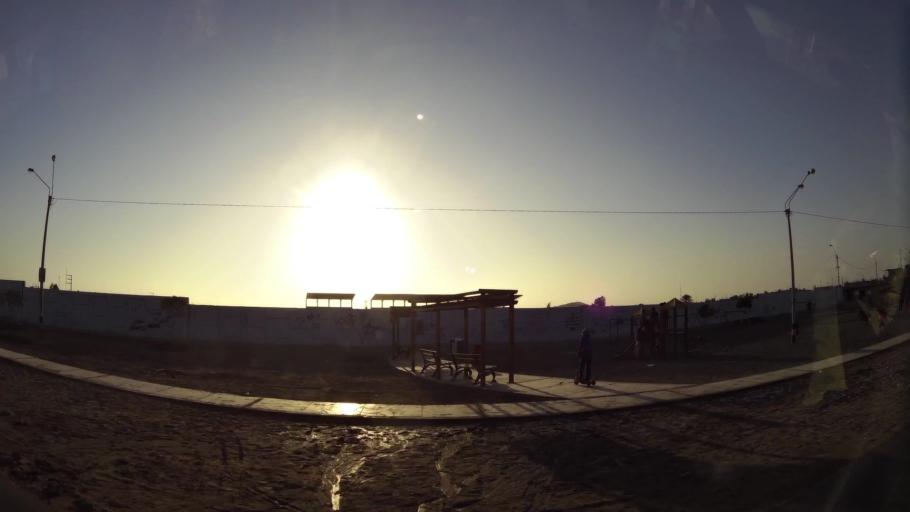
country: PE
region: Ica
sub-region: Provincia de Pisco
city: Villa Tupac Amaru
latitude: -13.7108
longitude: -76.1462
